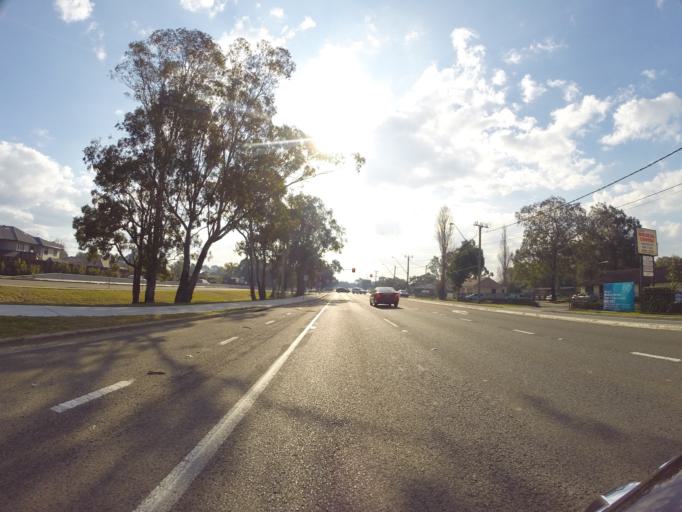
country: AU
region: New South Wales
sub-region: Bankstown
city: Milperra
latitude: -33.9498
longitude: 150.9506
